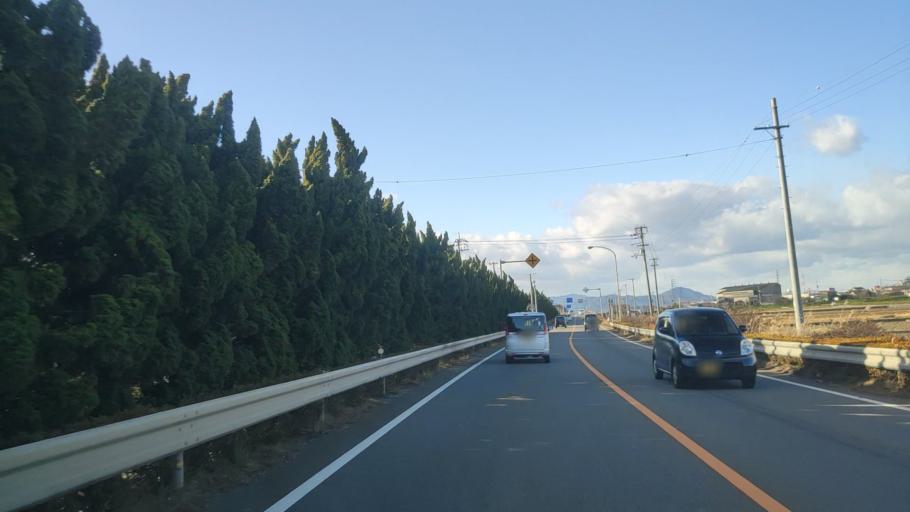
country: JP
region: Ehime
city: Saijo
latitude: 33.9165
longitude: 133.1293
